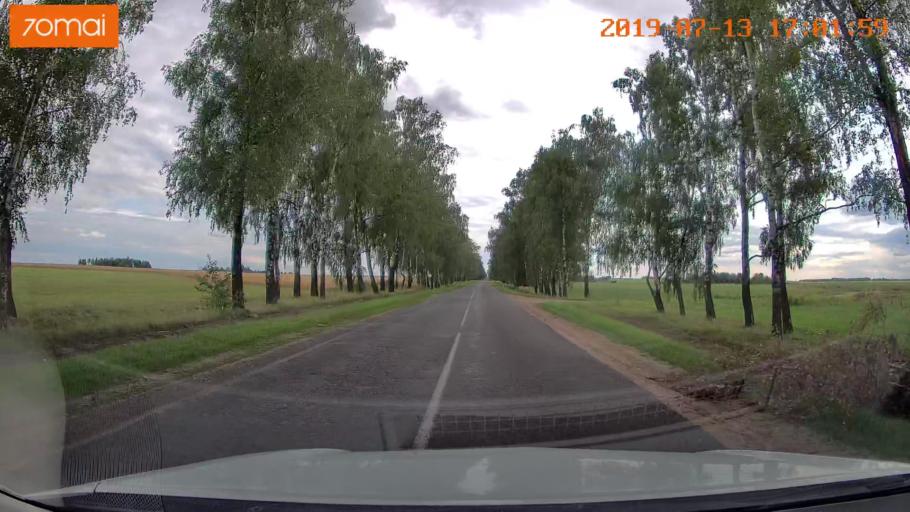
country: BY
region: Mogilev
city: Kirawsk
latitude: 53.2905
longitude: 29.3914
